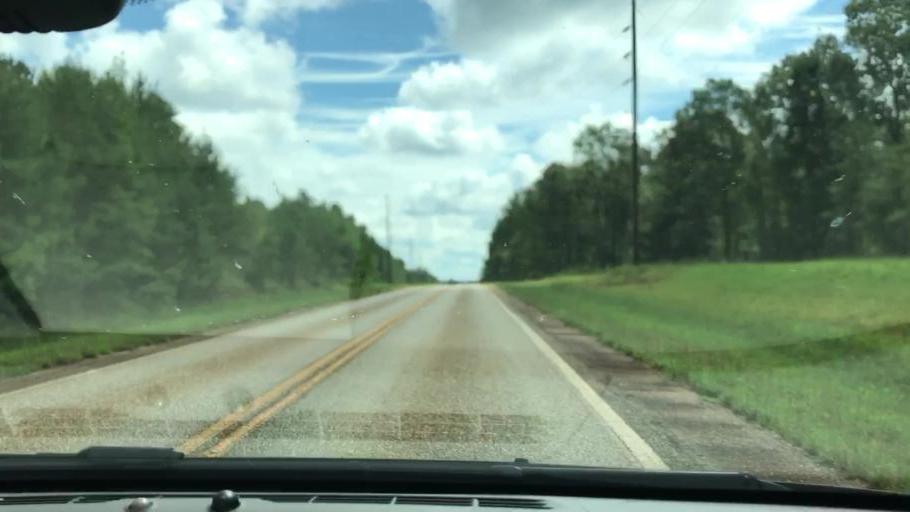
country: US
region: Georgia
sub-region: Stewart County
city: Lumpkin
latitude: 32.0624
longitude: -84.8315
